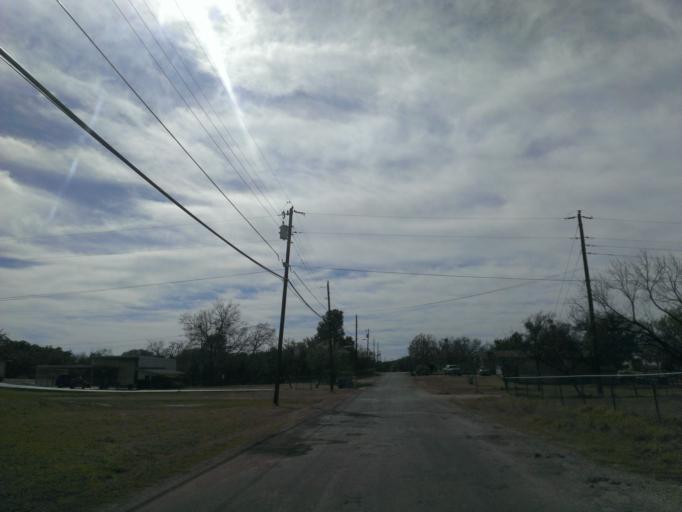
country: US
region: Texas
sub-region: Burnet County
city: Granite Shoals
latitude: 30.5811
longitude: -98.3881
